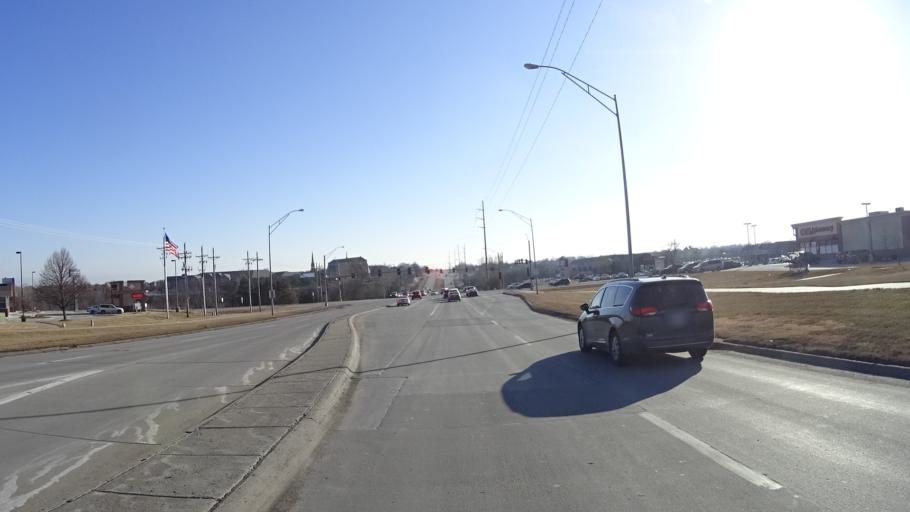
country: US
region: Nebraska
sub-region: Douglas County
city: Bennington
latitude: 41.2935
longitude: -96.1390
